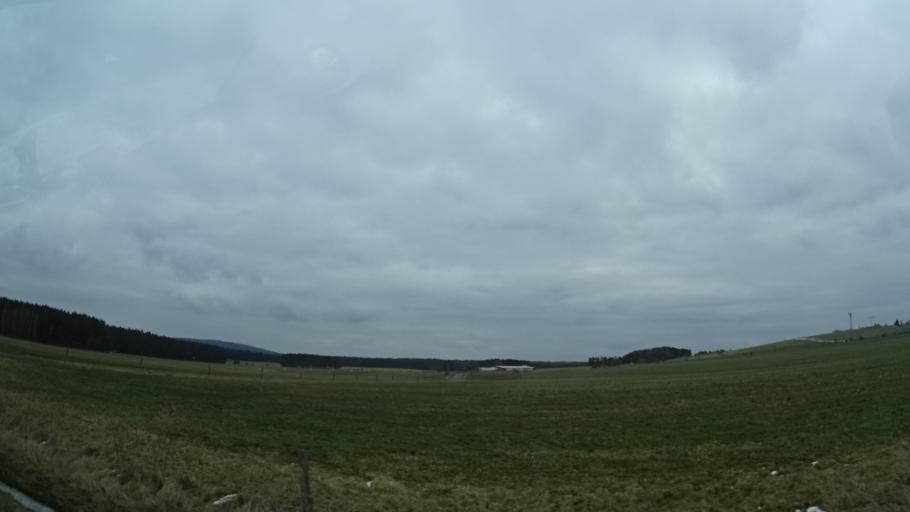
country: DE
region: Thuringia
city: Pennewitz
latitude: 50.6658
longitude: 11.0442
